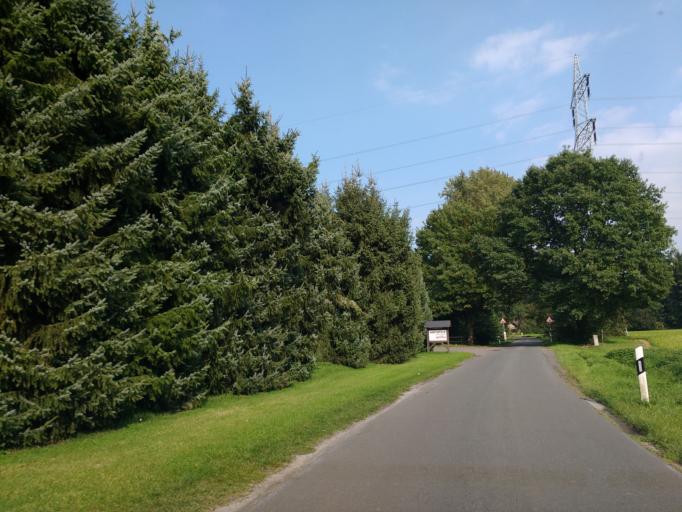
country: DE
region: North Rhine-Westphalia
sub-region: Regierungsbezirk Detmold
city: Hovelhof
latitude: 51.7834
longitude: 8.6966
